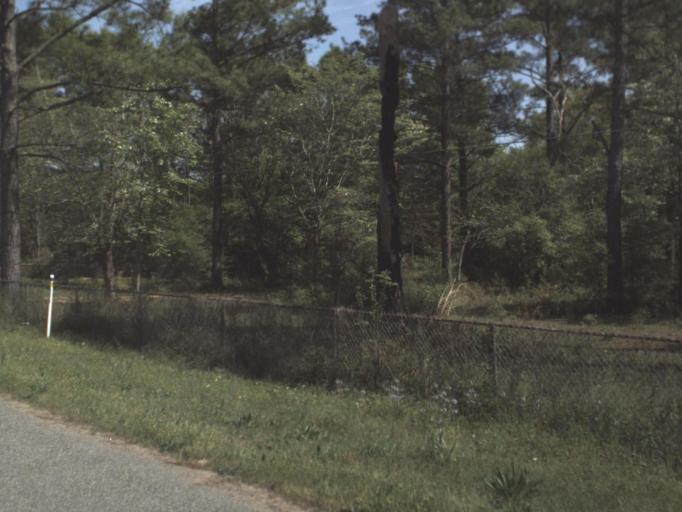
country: US
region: Florida
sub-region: Okaloosa County
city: Crestview
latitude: 30.7240
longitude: -86.7140
